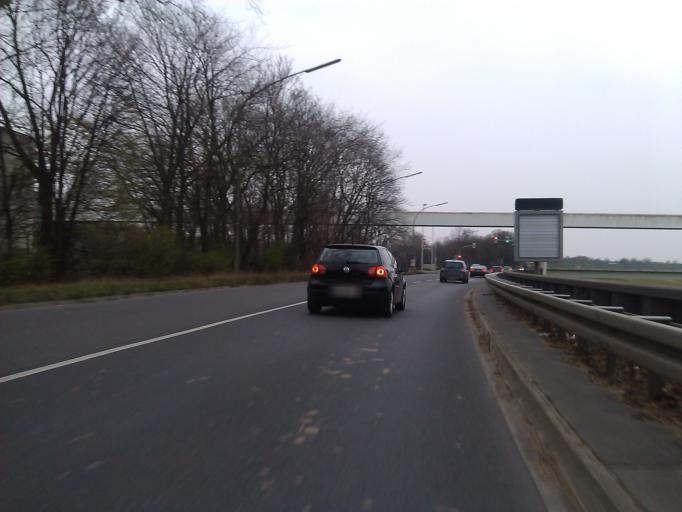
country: DE
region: North Rhine-Westphalia
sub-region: Regierungsbezirk Dusseldorf
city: Dormagen
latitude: 51.0791
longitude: 6.8500
